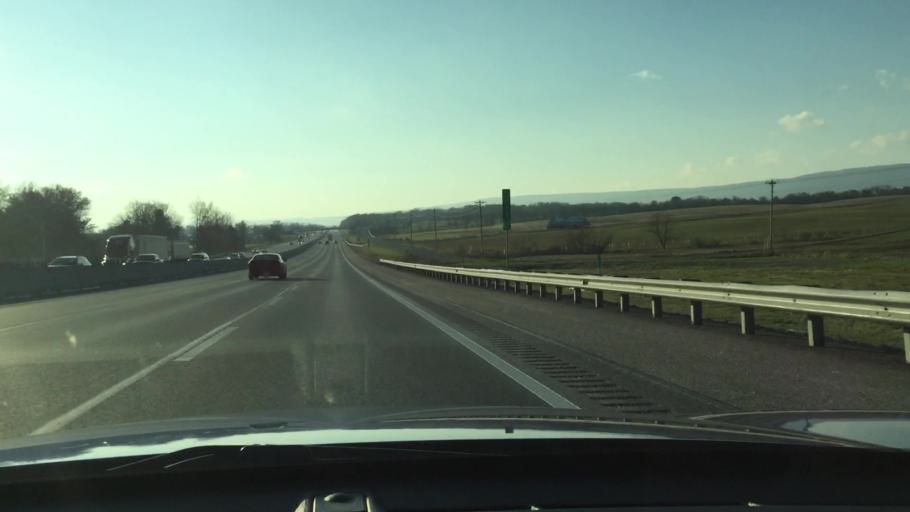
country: US
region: Pennsylvania
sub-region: Cumberland County
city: Newville
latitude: 40.1941
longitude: -77.4263
